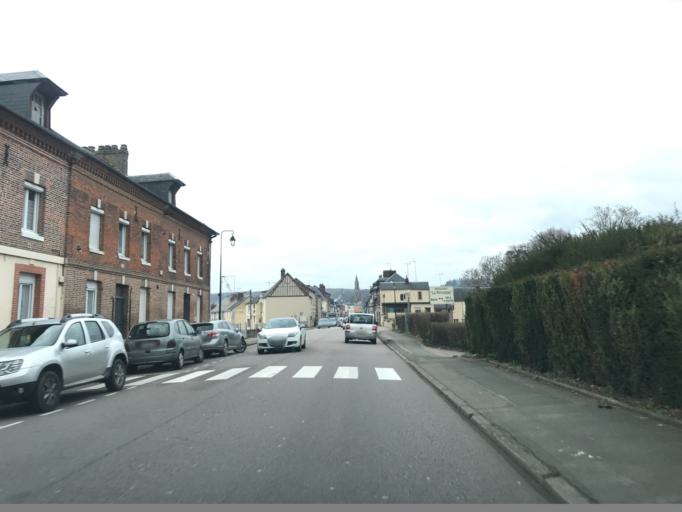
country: FR
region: Haute-Normandie
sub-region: Departement de l'Eure
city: Fleury-sur-Andelle
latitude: 49.3585
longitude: 1.3590
